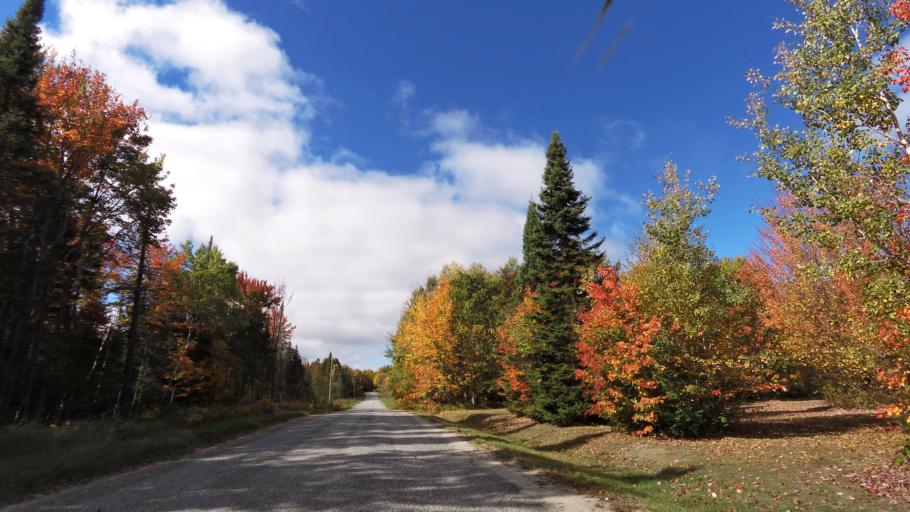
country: CA
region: Ontario
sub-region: Nipissing District
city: North Bay
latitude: 46.3760
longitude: -79.4882
